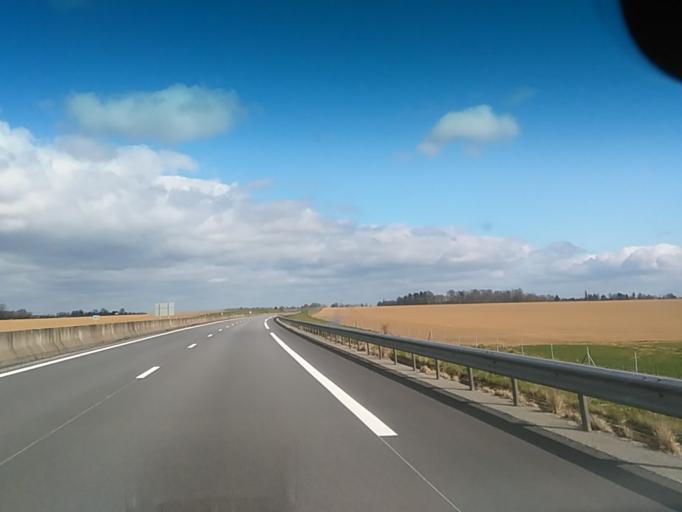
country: FR
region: Lower Normandy
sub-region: Departement du Calvados
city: Orbec
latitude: 49.0470
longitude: 0.4507
